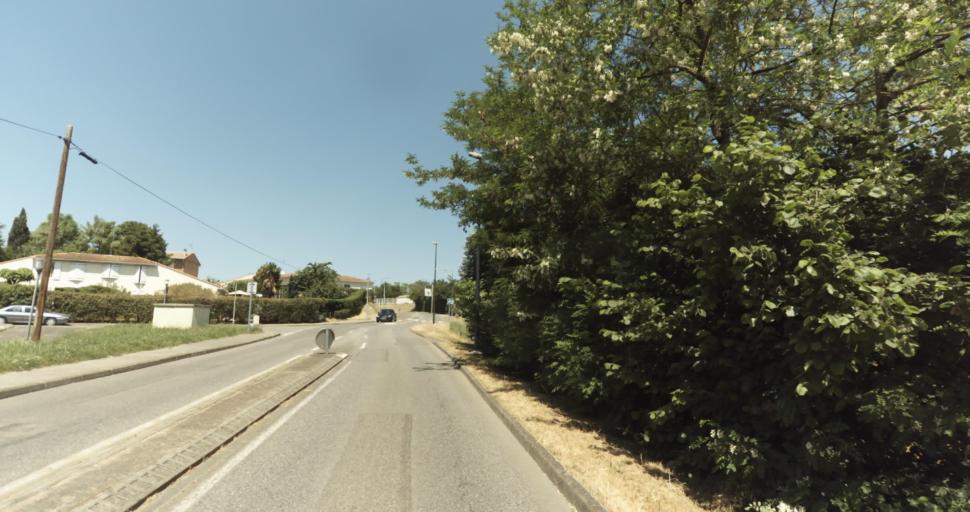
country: FR
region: Midi-Pyrenees
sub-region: Departement de la Haute-Garonne
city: Leguevin
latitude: 43.5959
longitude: 1.2313
